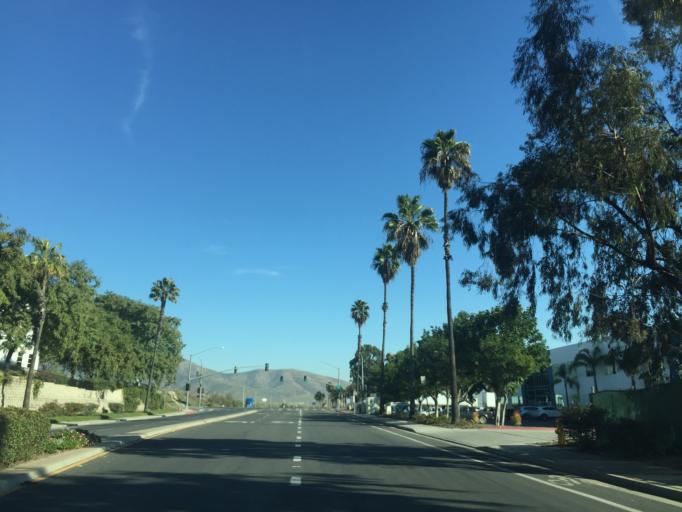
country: MX
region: Baja California
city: Tijuana
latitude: 32.5568
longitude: -116.9293
